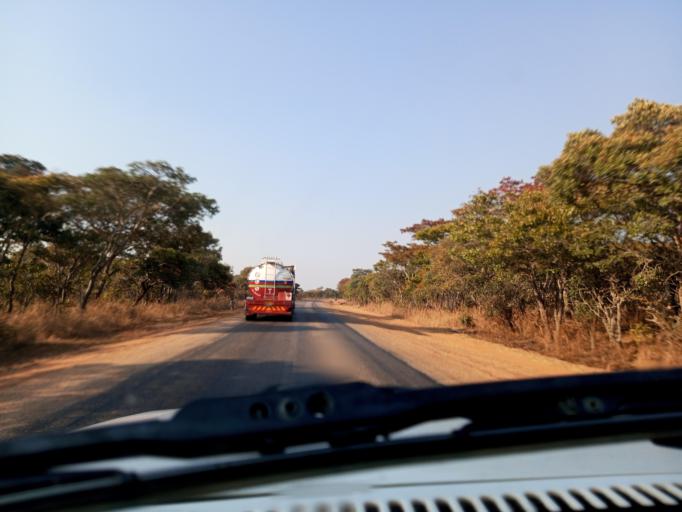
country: ZM
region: Northern
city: Mpika
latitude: -12.3653
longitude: 31.1038
